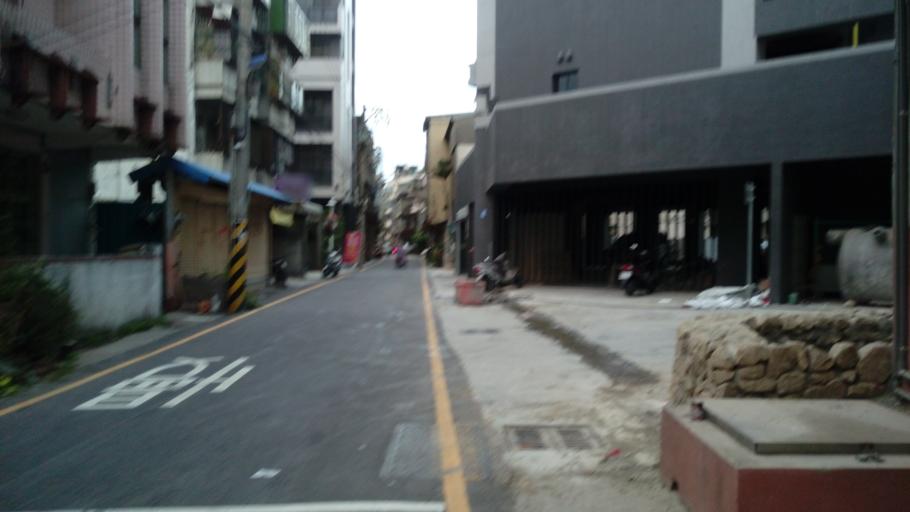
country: TW
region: Taiwan
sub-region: Hsinchu
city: Hsinchu
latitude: 24.8049
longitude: 120.9497
